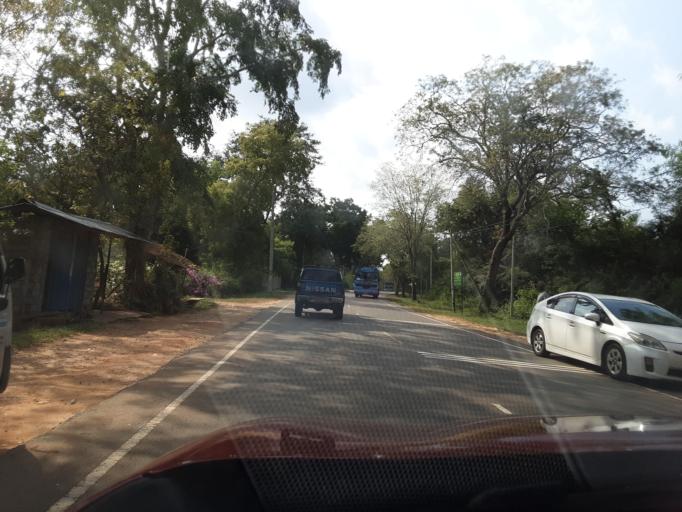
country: LK
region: Uva
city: Haputale
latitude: 6.3625
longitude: 81.1797
